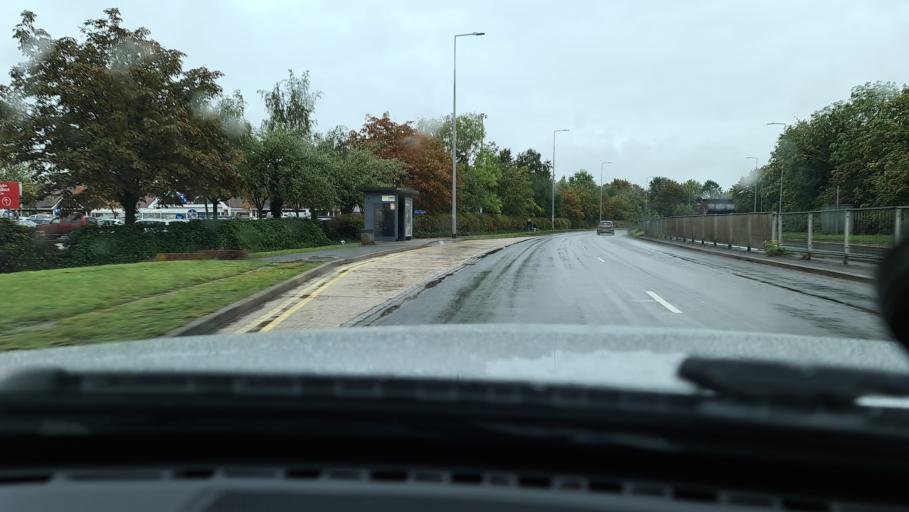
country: GB
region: England
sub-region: Buckinghamshire
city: Bletchley
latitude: 52.0023
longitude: -0.7262
